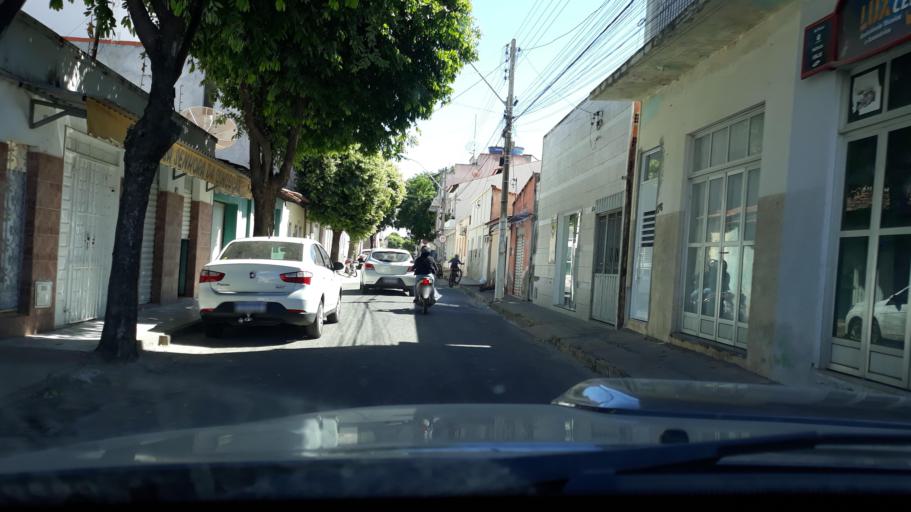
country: BR
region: Bahia
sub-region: Guanambi
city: Guanambi
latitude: -14.2272
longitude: -42.7829
